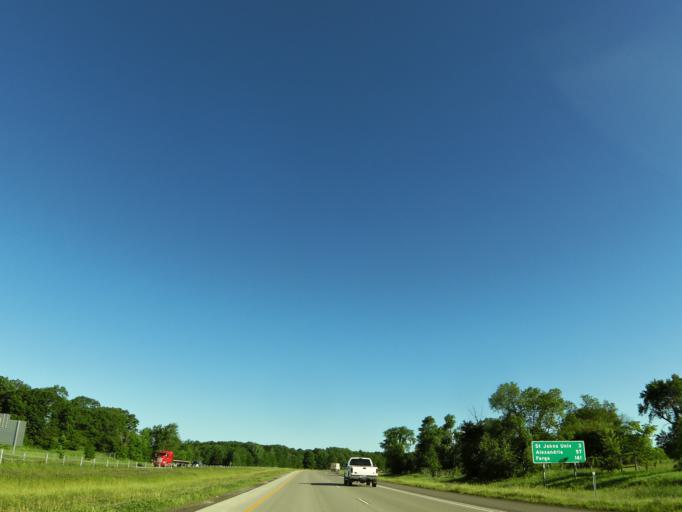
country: US
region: Minnesota
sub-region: Stearns County
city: Collegeville
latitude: 45.5688
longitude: -94.3527
